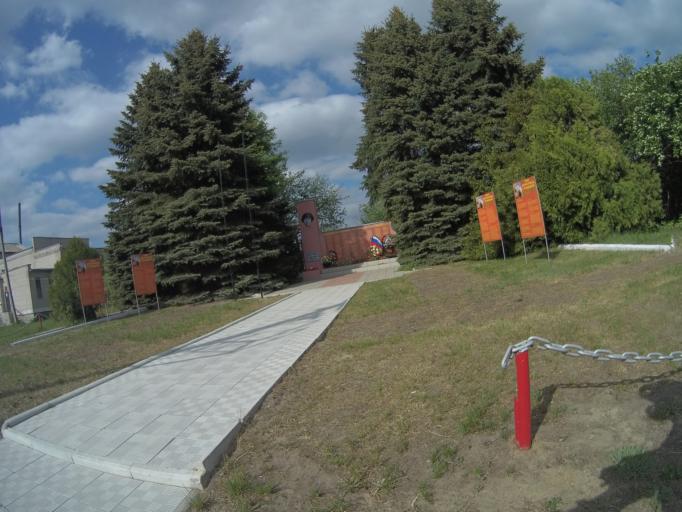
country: RU
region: Vladimir
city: Raduzhnyy
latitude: 55.9985
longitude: 40.2099
